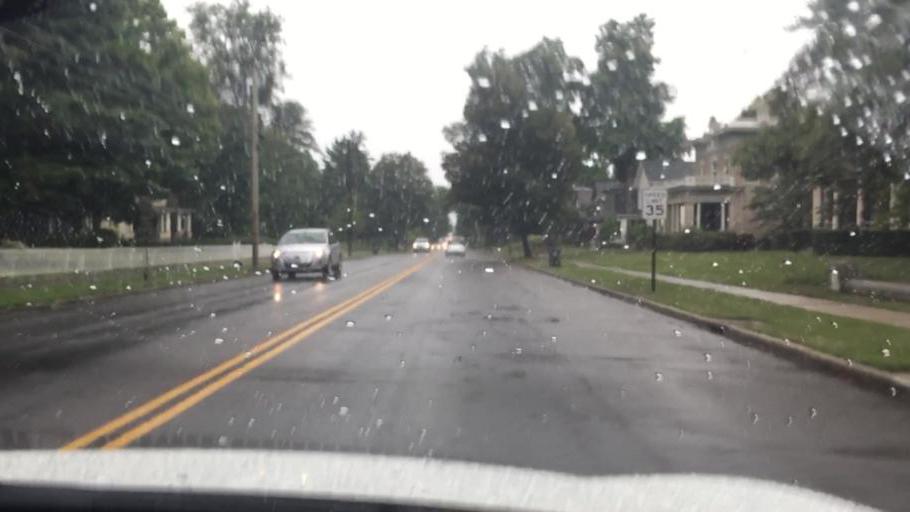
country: US
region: Ohio
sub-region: Champaign County
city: Urbana
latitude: 40.1077
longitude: -83.7434
